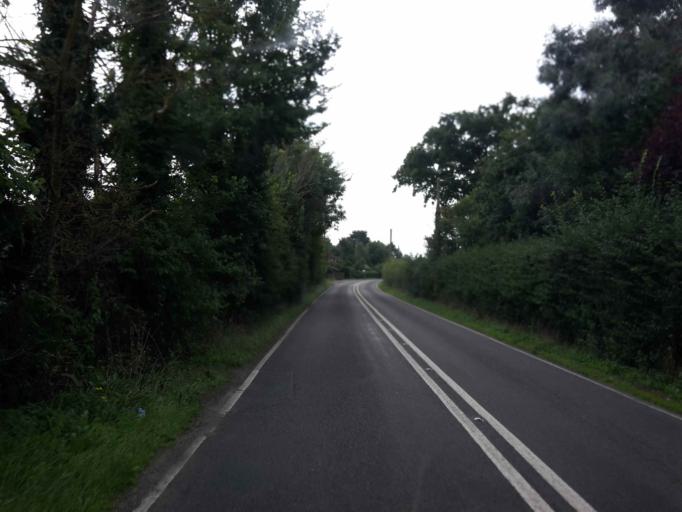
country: GB
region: England
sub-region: West Sussex
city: Billingshurst
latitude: 50.9896
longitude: -0.4072
